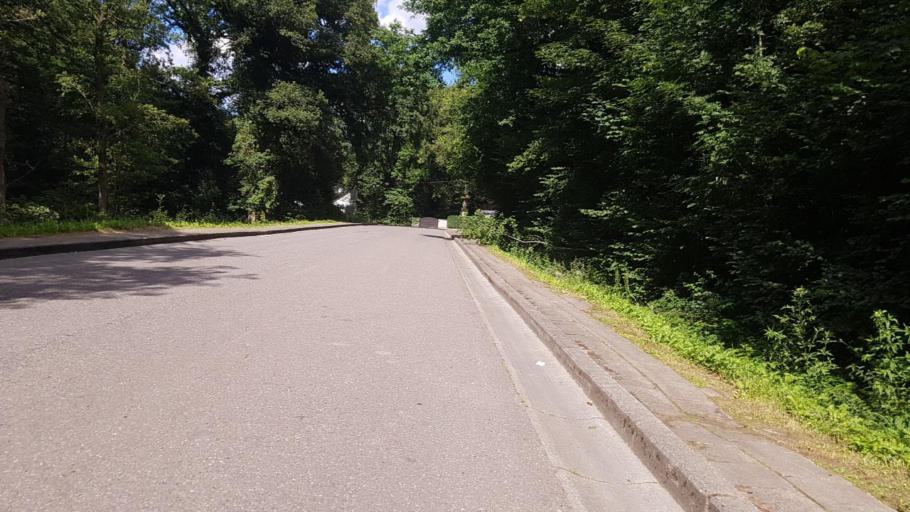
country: BE
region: Wallonia
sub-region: Province du Hainaut
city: Charleroi
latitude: 50.3550
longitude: 4.4320
